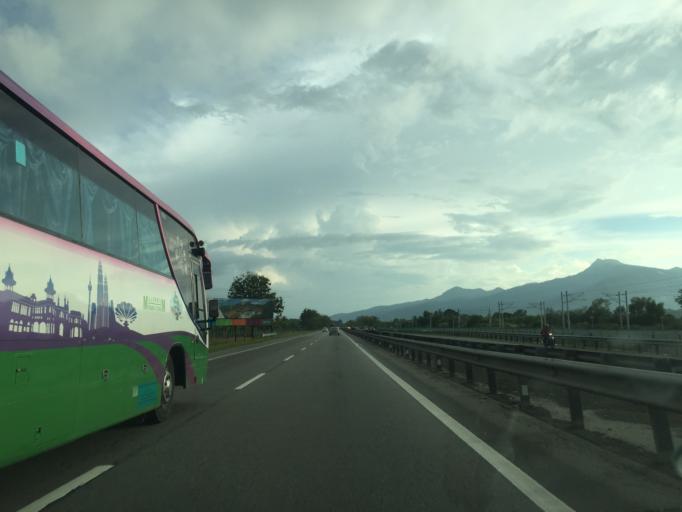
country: MY
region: Kedah
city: Gurun
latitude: 5.8826
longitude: 100.4774
